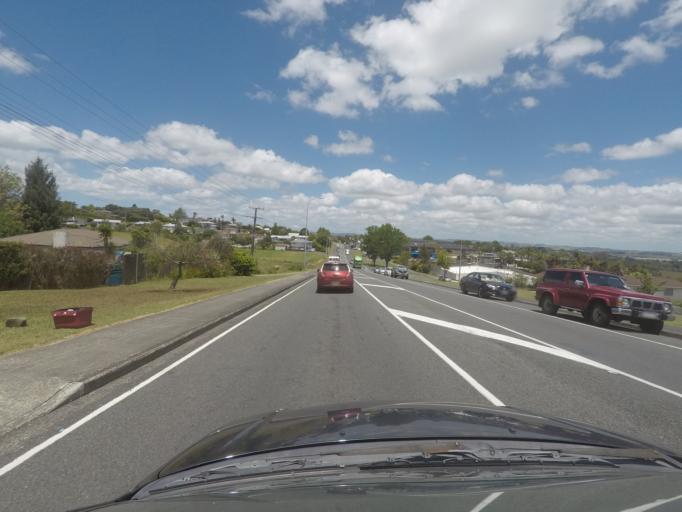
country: NZ
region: Northland
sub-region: Whangarei
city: Whangarei
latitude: -35.7522
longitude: 174.3681
